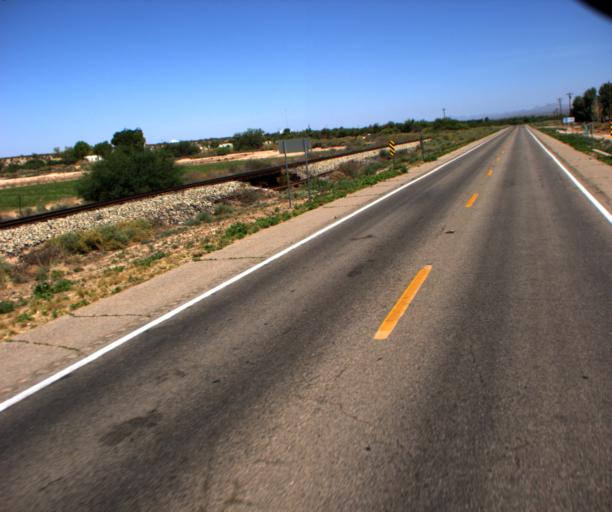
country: US
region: Arizona
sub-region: Graham County
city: Pima
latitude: 33.0176
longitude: -109.9532
